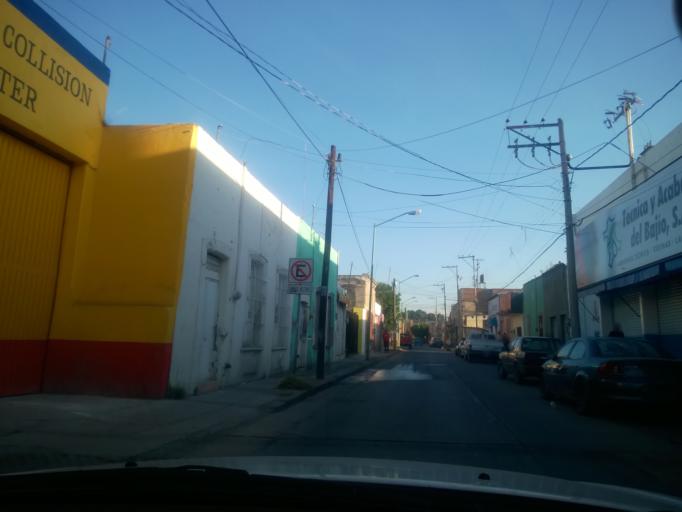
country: MX
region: Guanajuato
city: Leon
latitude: 21.1308
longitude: -101.6818
